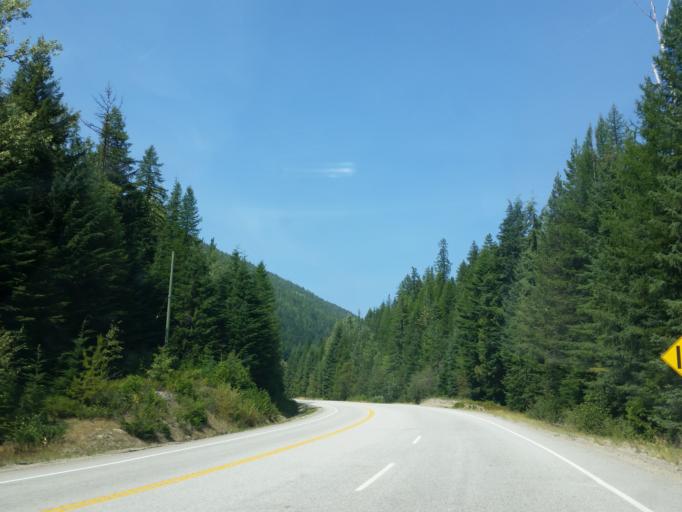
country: CA
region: British Columbia
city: Castlegar
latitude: 49.2779
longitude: -117.7221
